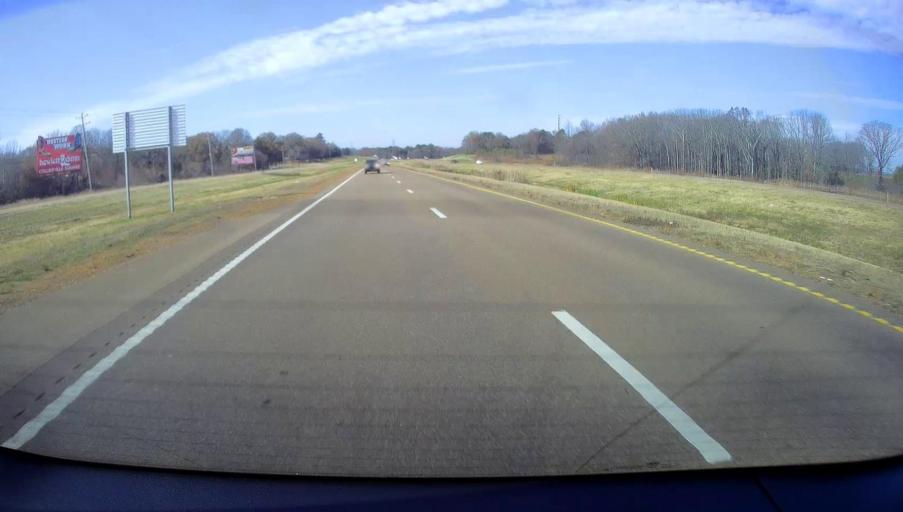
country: US
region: Tennessee
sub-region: Fayette County
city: Piperton
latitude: 34.9874
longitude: -89.6036
